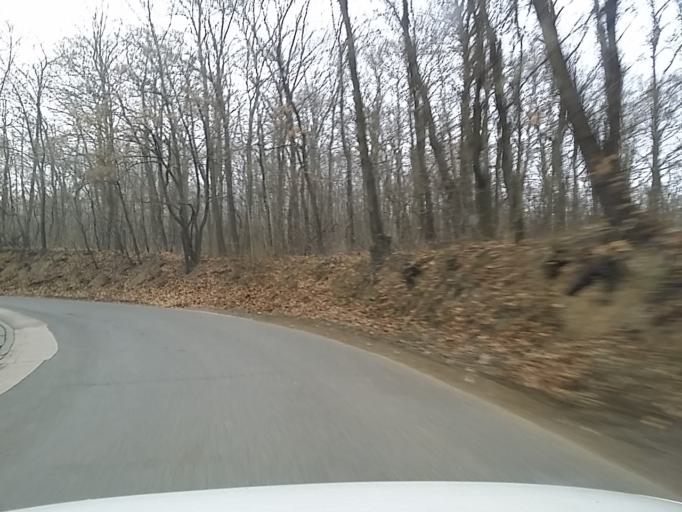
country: HU
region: Pest
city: Budakeszi
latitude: 47.5403
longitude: 18.9495
